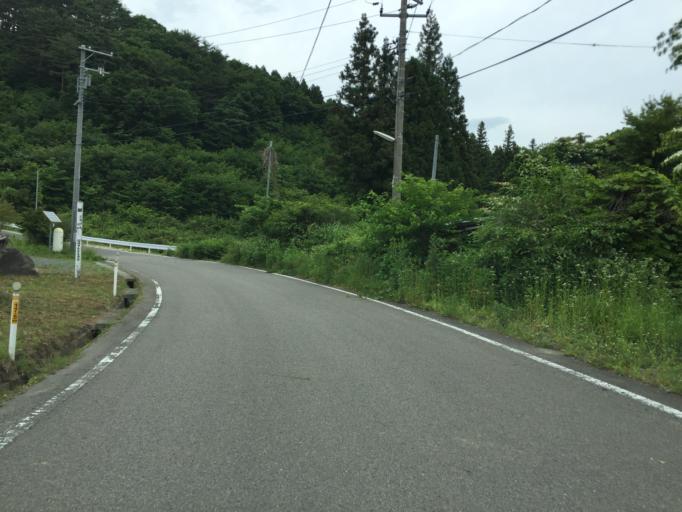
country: JP
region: Fukushima
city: Funehikimachi-funehiki
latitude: 37.4251
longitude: 140.7364
